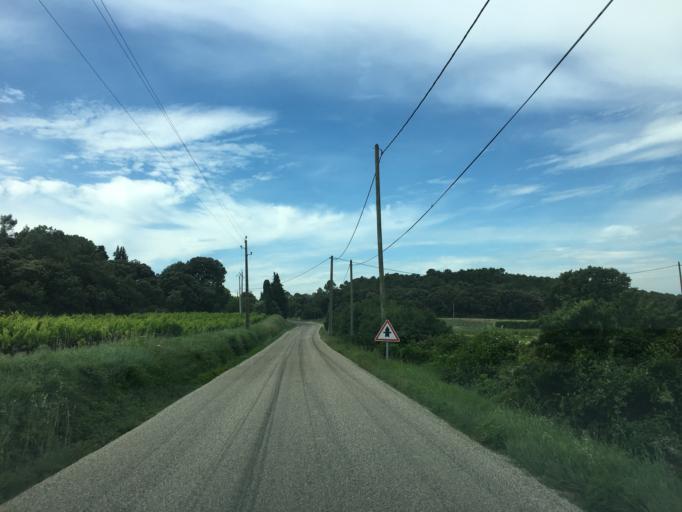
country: FR
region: Provence-Alpes-Cote d'Azur
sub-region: Departement du Vaucluse
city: Bollene
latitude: 44.2987
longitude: 4.7676
